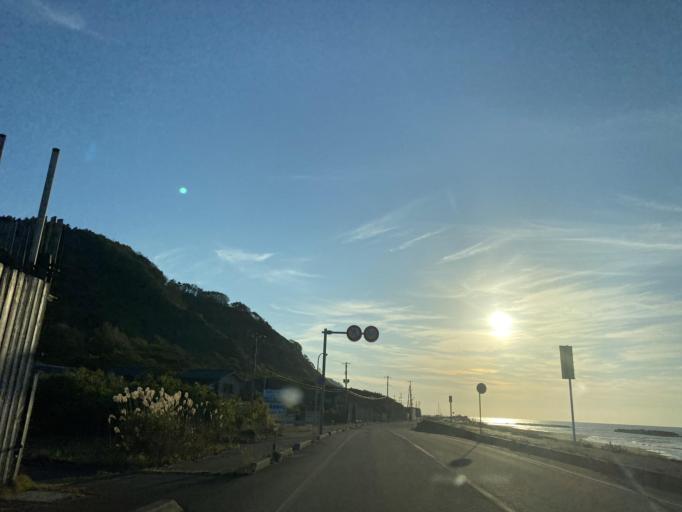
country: JP
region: Niigata
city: Kashiwazaki
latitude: 37.4976
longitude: 138.6397
